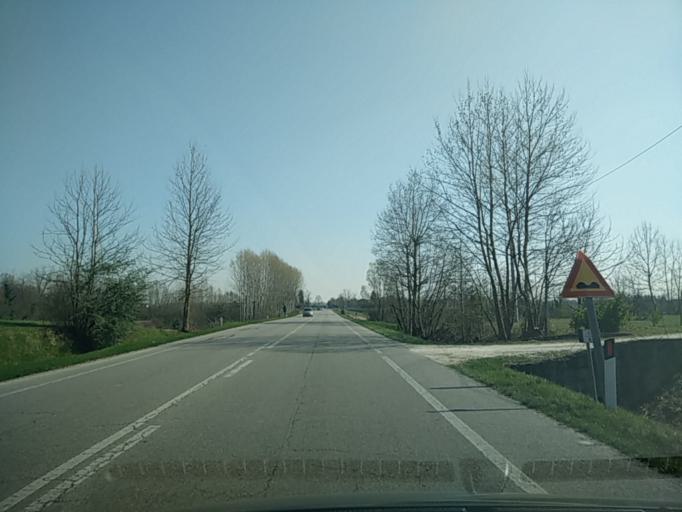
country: IT
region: Friuli Venezia Giulia
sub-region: Provincia di Pordenone
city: Cecchini
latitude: 45.8597
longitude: 12.6301
